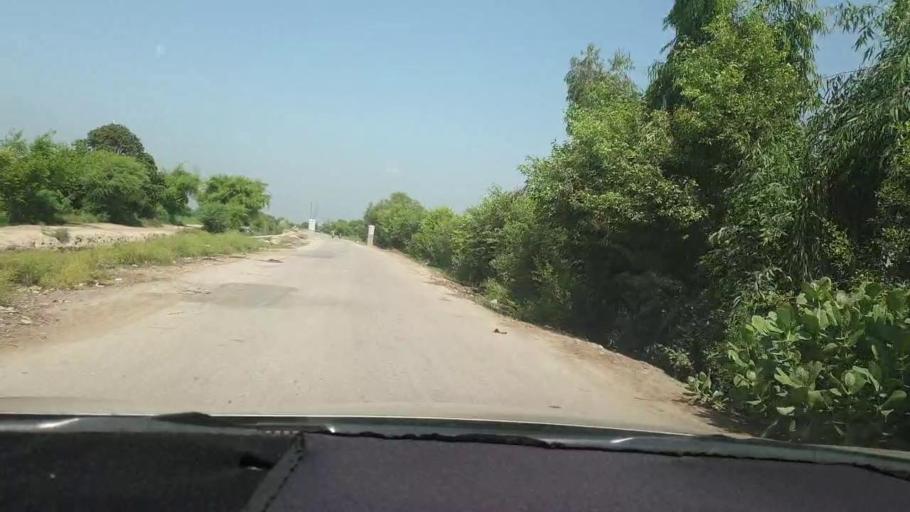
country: PK
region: Sindh
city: Miro Khan
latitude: 27.7587
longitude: 68.0802
